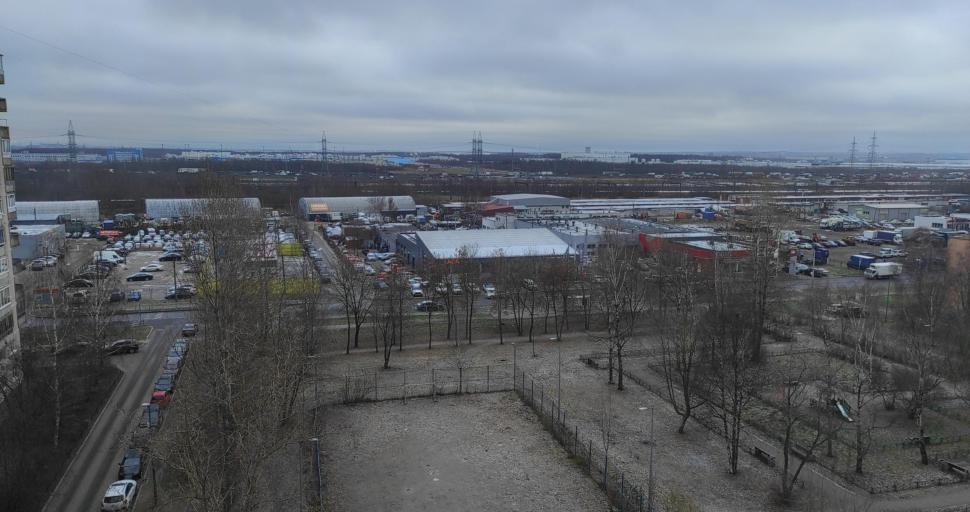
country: RU
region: St.-Petersburg
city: Obukhovo
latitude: 59.8303
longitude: 30.4269
